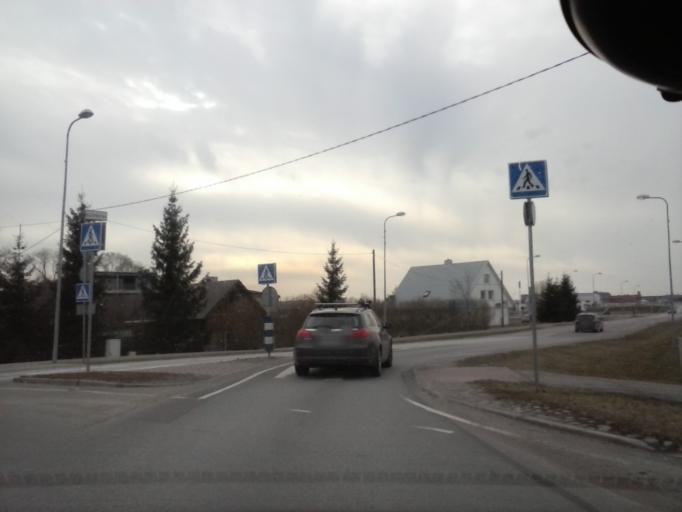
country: EE
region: Harju
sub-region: Rae vald
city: Jueri
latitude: 59.3560
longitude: 24.8967
